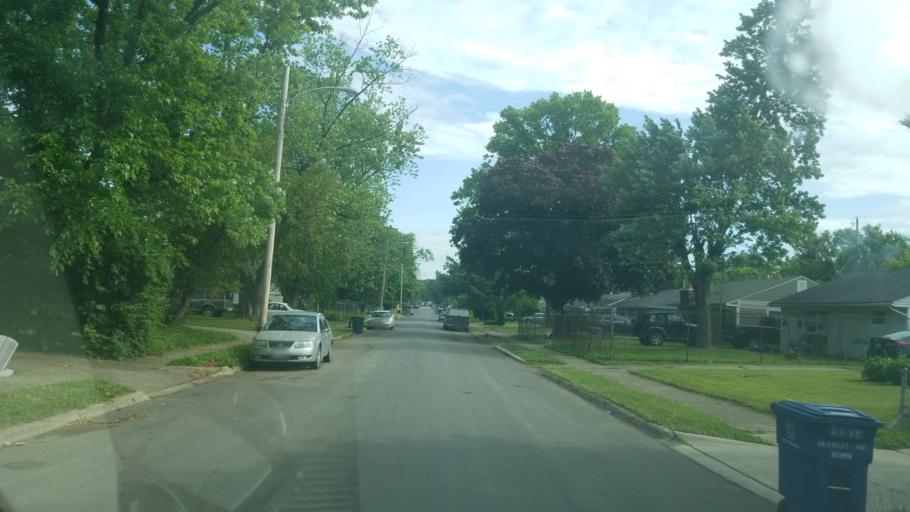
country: US
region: Ohio
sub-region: Franklin County
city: Minerva Park
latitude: 40.0368
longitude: -82.9755
